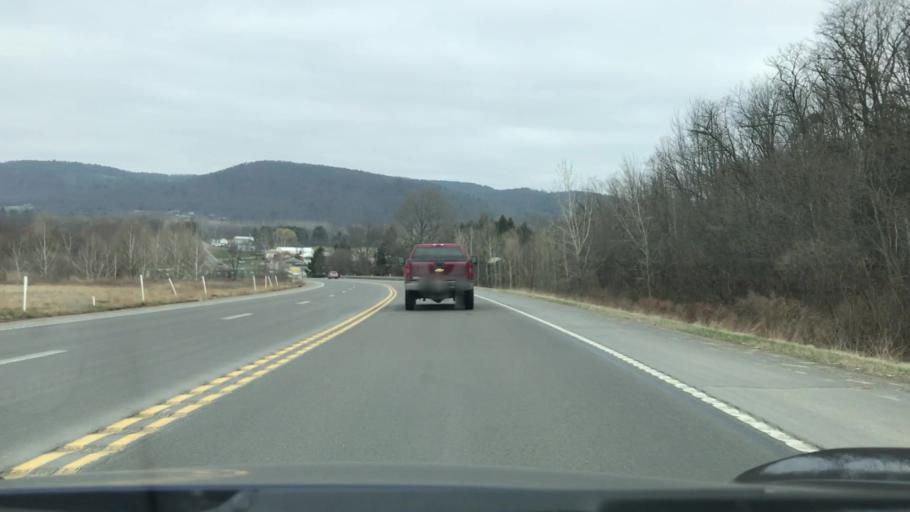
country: US
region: Pennsylvania
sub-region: Bradford County
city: Towanda
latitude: 41.7727
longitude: -76.3712
